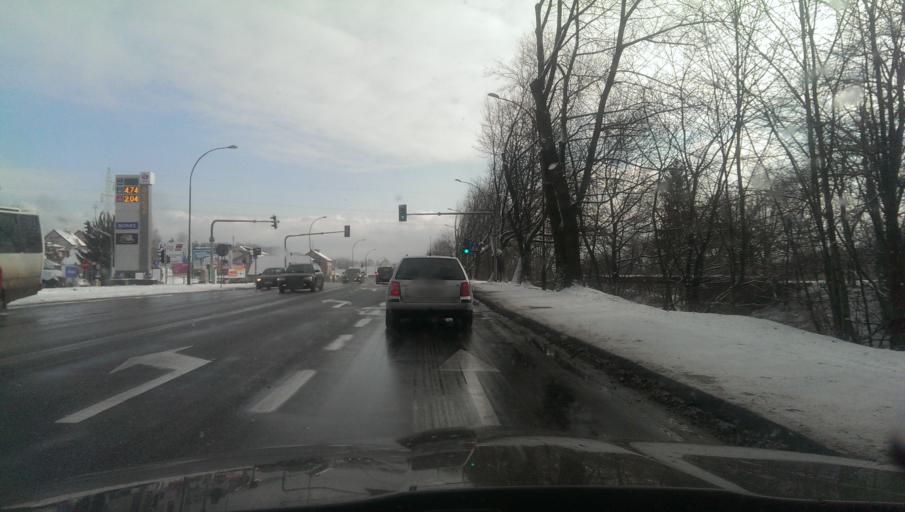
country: PL
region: Subcarpathian Voivodeship
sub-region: Powiat sanocki
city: Sanok
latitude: 49.5643
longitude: 22.1806
